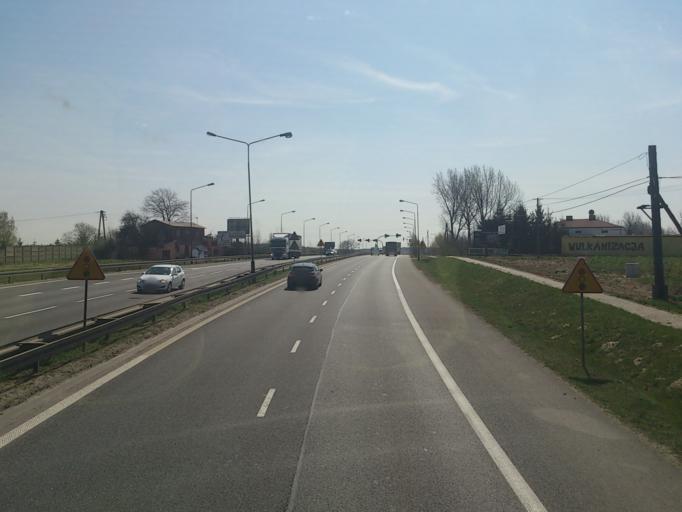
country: PL
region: Lodz Voivodeship
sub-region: Powiat lodzki wschodni
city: Tuszyn
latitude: 51.5667
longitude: 19.5844
